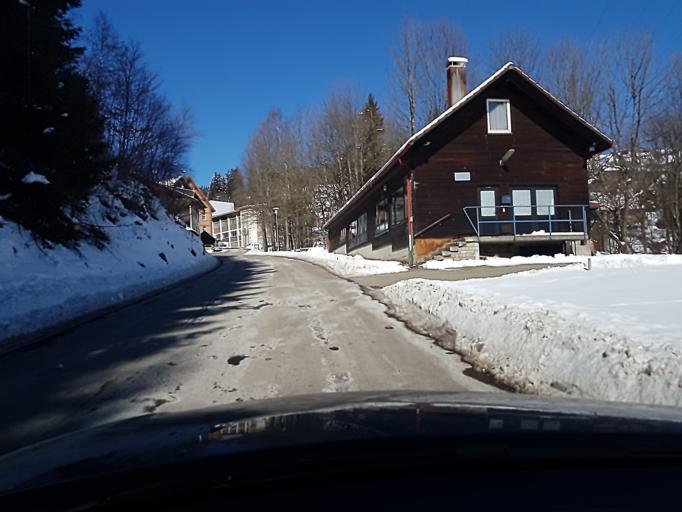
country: DE
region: Baden-Wuerttemberg
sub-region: Freiburg Region
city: Schonach im Schwarzwald
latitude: 48.1402
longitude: 8.2071
